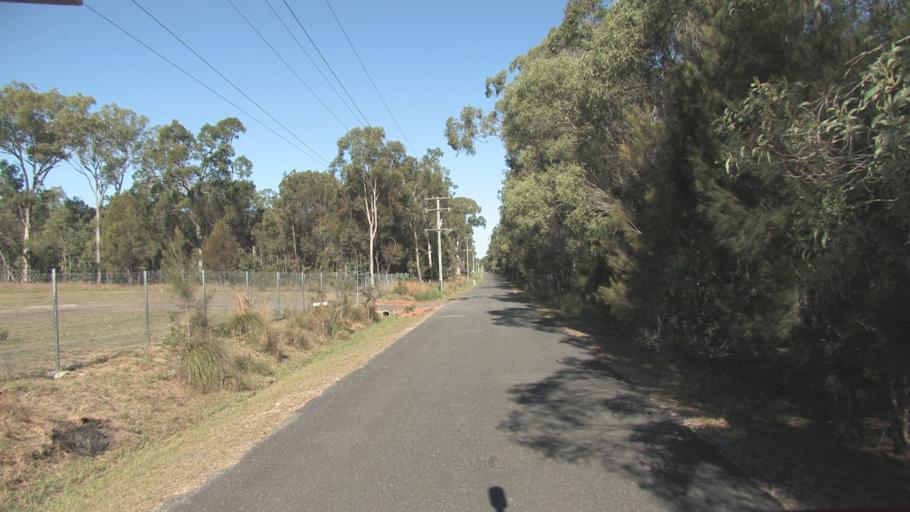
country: AU
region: Queensland
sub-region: Logan
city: Park Ridge South
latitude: -27.6886
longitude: 153.0059
